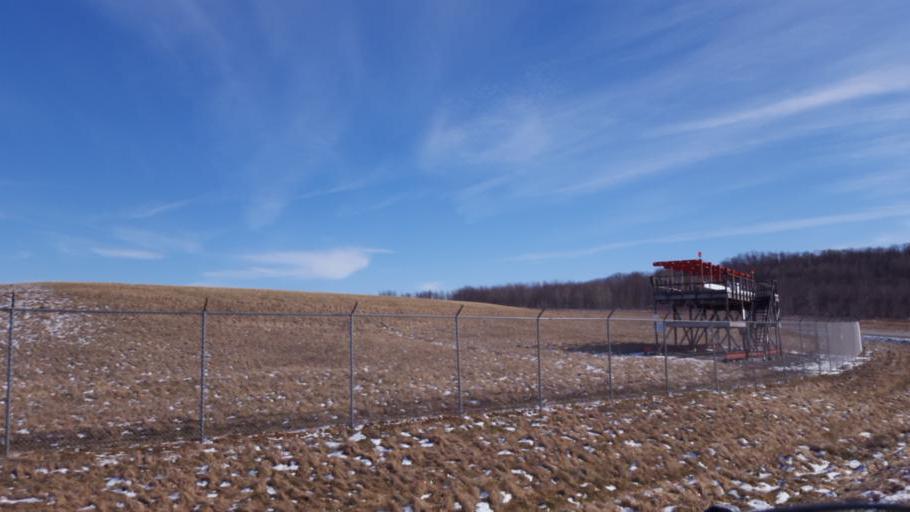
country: US
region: New York
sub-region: Allegany County
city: Wellsville
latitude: 42.1099
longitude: -78.0007
